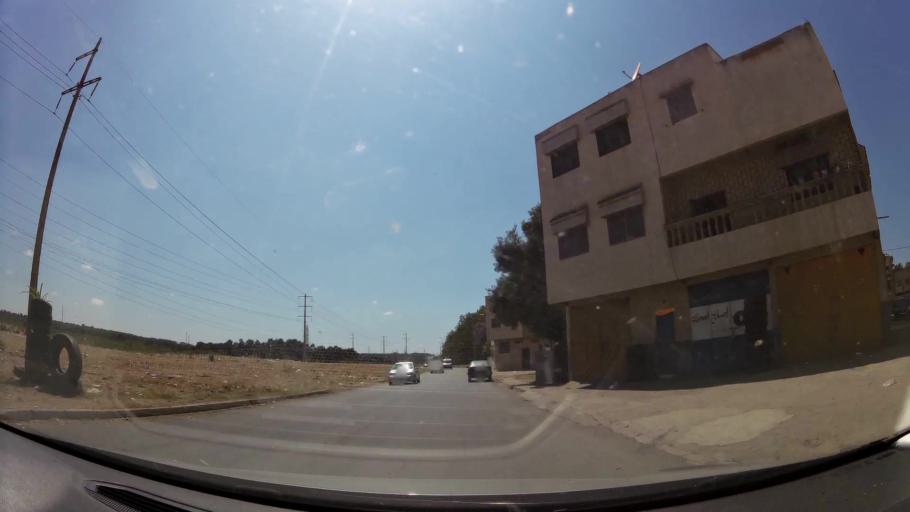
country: MA
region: Gharb-Chrarda-Beni Hssen
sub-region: Kenitra Province
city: Kenitra
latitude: 34.2372
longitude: -6.5558
